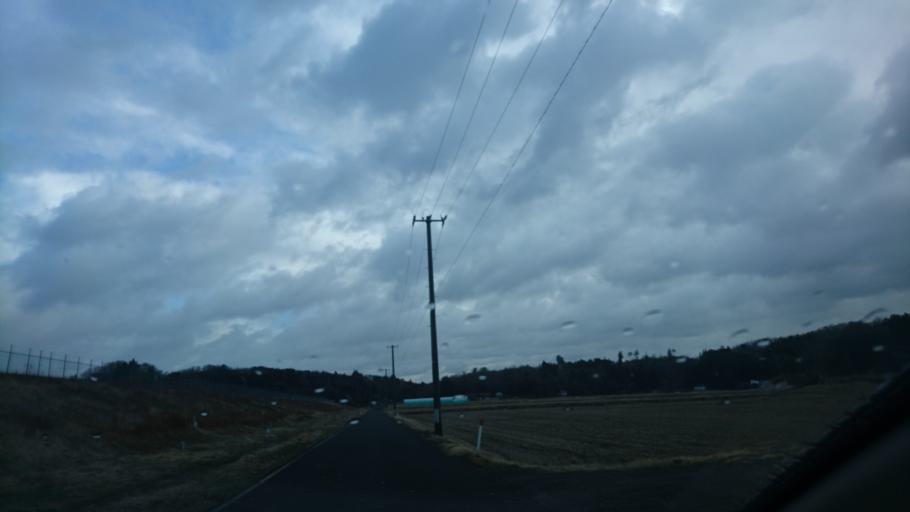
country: JP
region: Iwate
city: Ichinoseki
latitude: 38.7817
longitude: 141.0339
